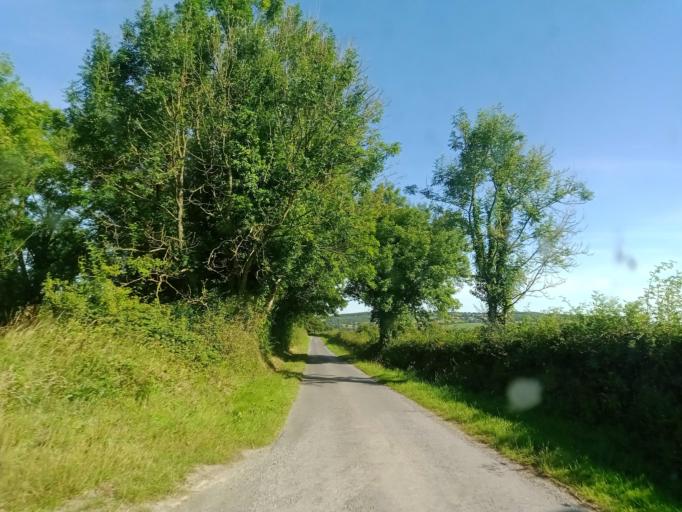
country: IE
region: Leinster
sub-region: Kilkenny
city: Ballyragget
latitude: 52.7928
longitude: -7.4244
